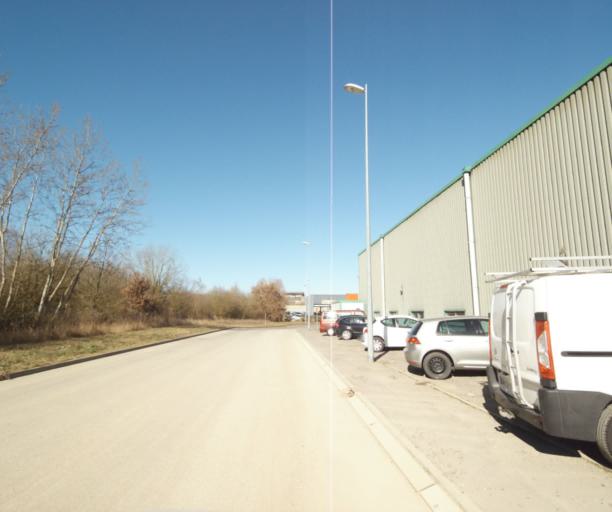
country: FR
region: Lorraine
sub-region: Departement de Meurthe-et-Moselle
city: Fleville-devant-Nancy
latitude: 48.6108
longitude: 6.2030
